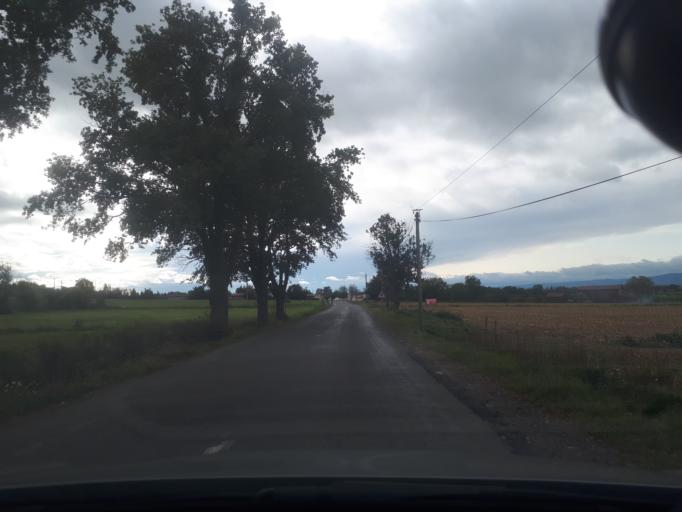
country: FR
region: Rhone-Alpes
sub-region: Departement de la Loire
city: Bellegarde-en-Forez
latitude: 45.6628
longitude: 4.2921
